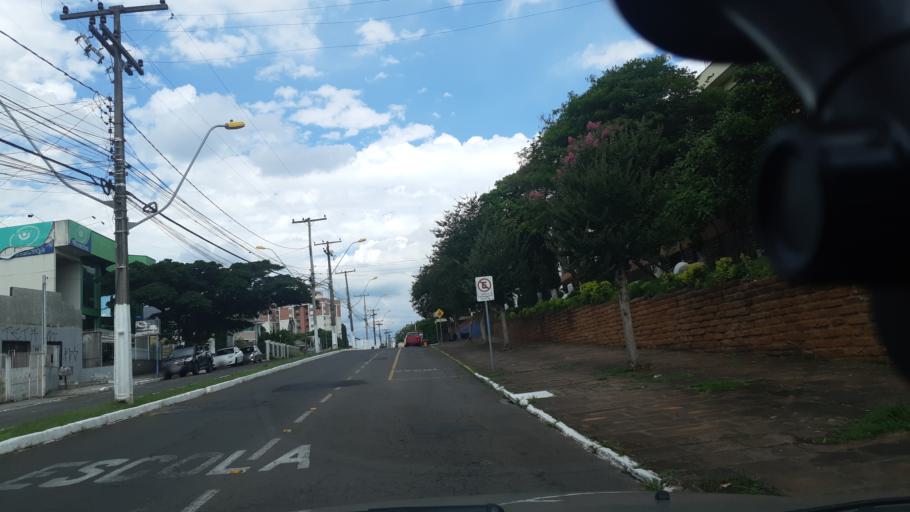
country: BR
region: Rio Grande do Sul
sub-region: Esteio
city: Esteio
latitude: -29.8492
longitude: -51.1629
